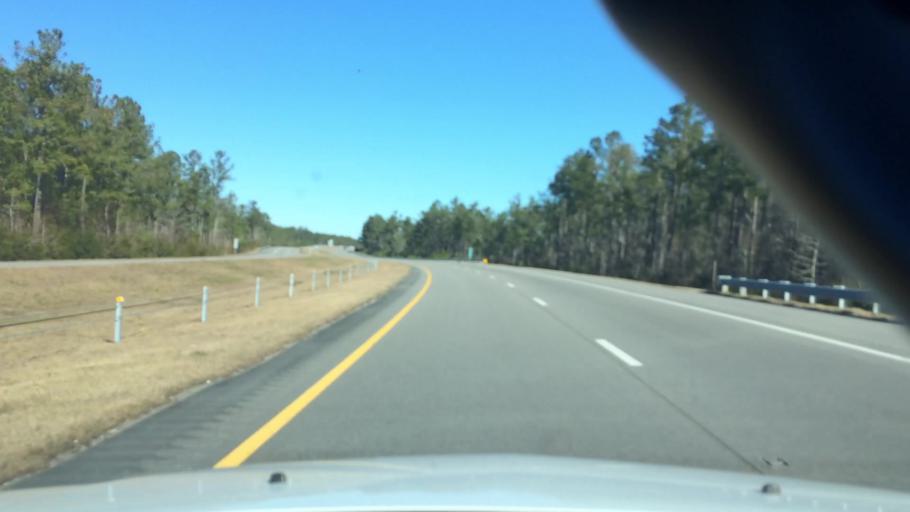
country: US
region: North Carolina
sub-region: Brunswick County
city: Leland
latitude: 34.2107
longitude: -78.0763
